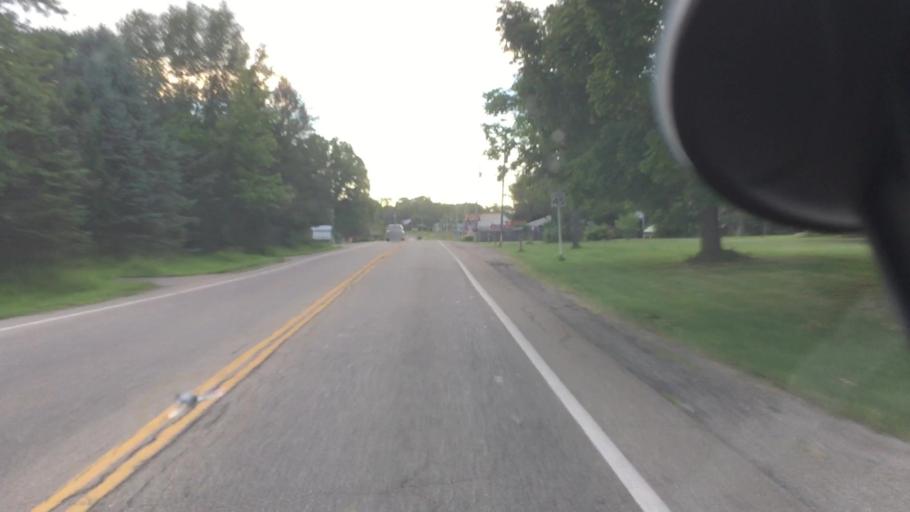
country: US
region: Ohio
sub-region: Columbiana County
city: East Palestine
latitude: 40.8611
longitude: -80.5500
